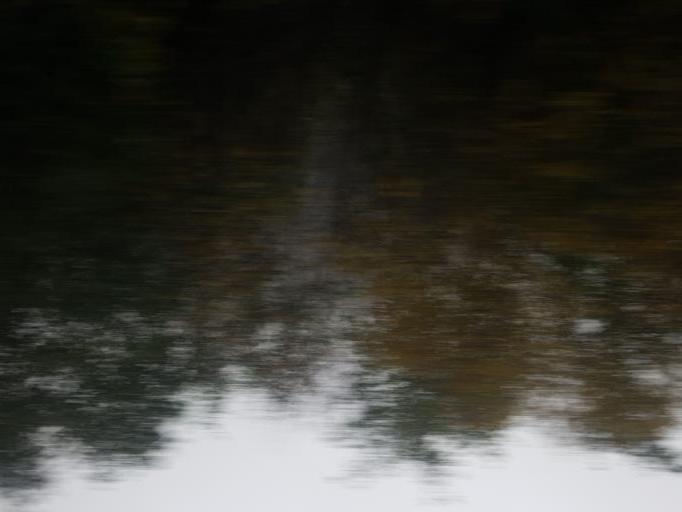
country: NO
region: Sor-Trondelag
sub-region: Trondheim
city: Trondheim
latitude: 63.3707
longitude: 10.3618
